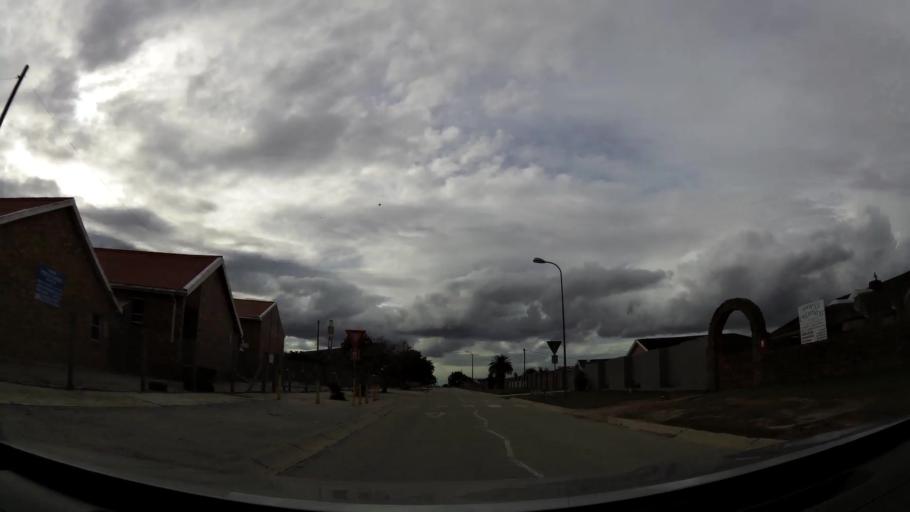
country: ZA
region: Eastern Cape
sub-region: Nelson Mandela Bay Metropolitan Municipality
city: Port Elizabeth
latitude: -33.9442
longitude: 25.4944
